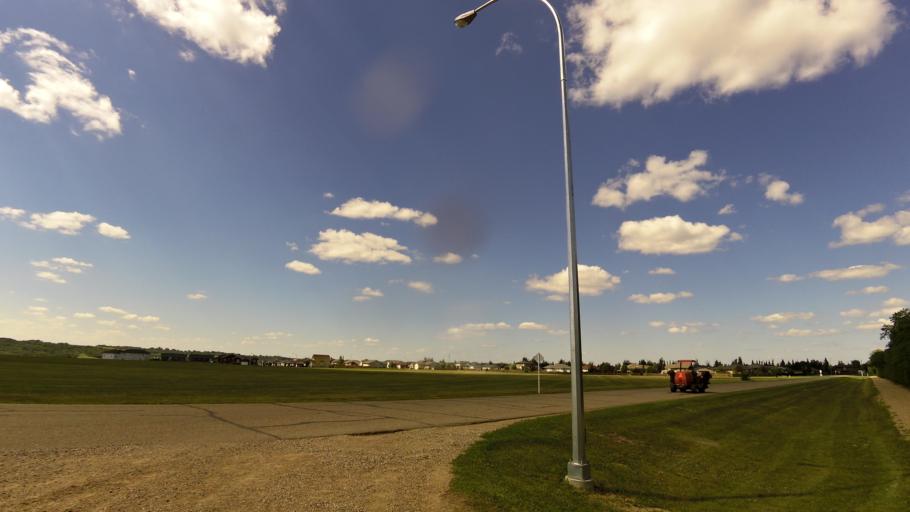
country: CA
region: Saskatchewan
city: North Battleford
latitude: 52.7269
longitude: -108.3004
